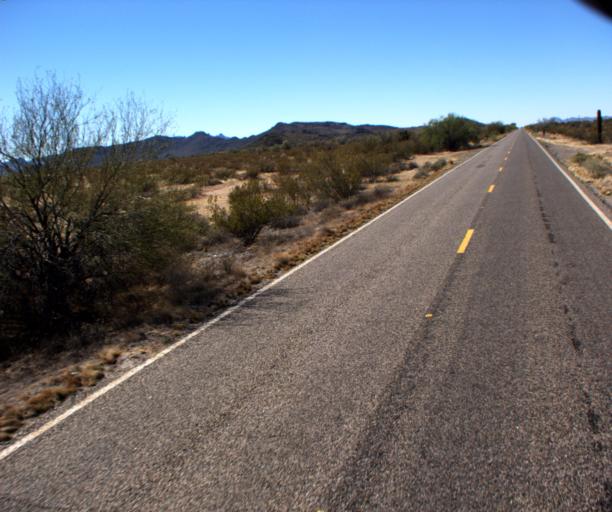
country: US
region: Arizona
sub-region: Pima County
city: Ajo
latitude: 32.2478
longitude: -112.7468
